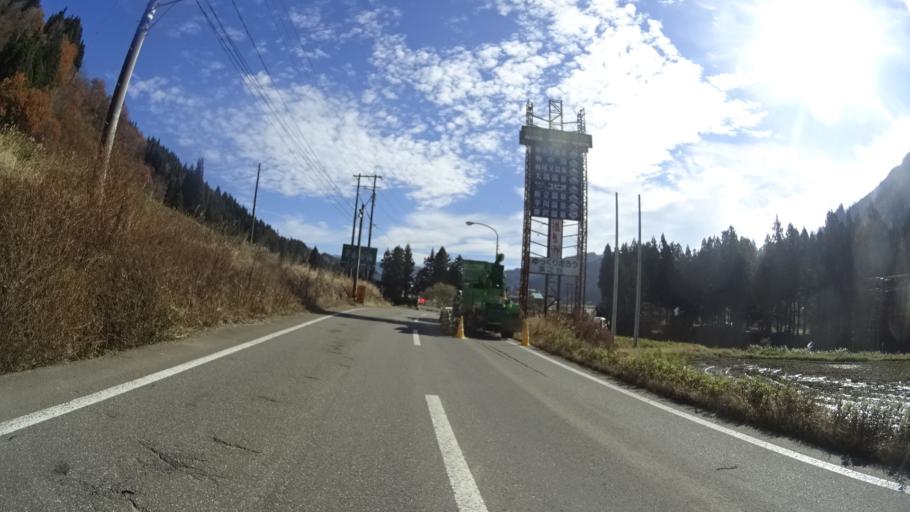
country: JP
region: Niigata
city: Muikamachi
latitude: 37.2199
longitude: 139.0321
